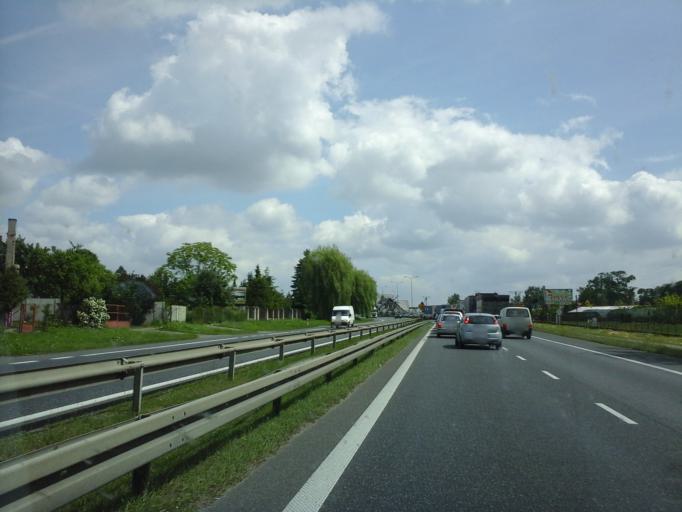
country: PL
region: Lodz Voivodeship
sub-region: Powiat lodzki wschodni
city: Tuszyn
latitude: 51.6018
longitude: 19.5395
